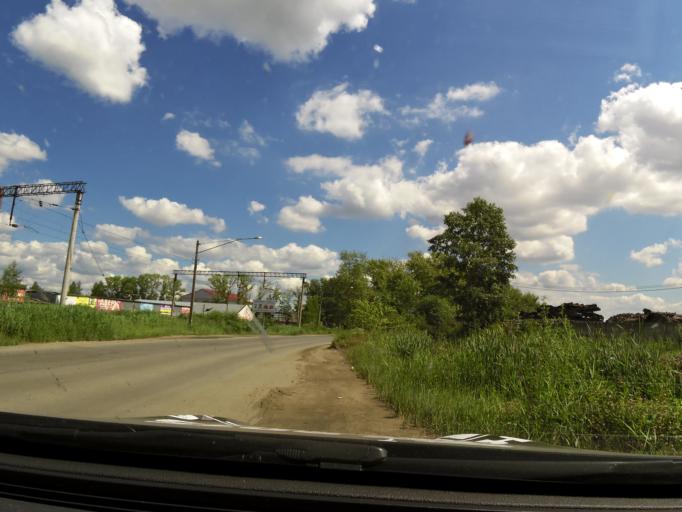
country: RU
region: Vologda
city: Vologda
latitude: 59.2328
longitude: 39.8392
